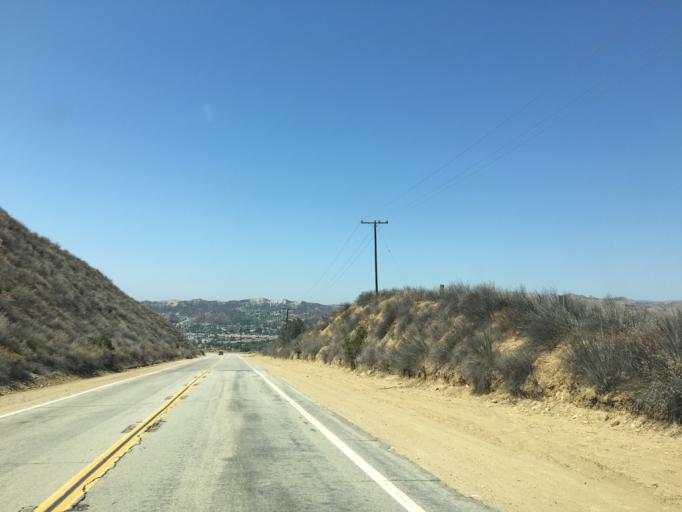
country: US
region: California
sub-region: Los Angeles County
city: Castaic
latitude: 34.5100
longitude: -118.5997
